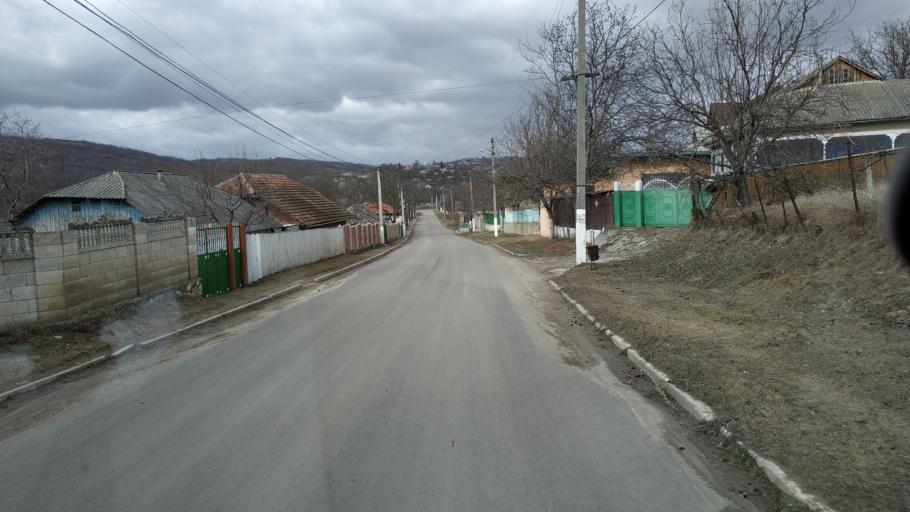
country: MD
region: Stinga Nistrului
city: Bucovat
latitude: 47.2292
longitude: 28.4312
